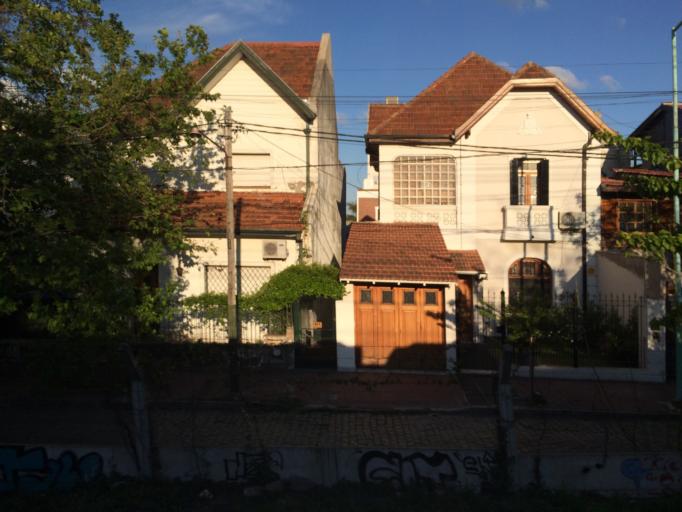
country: AR
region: Buenos Aires
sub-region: Partido de Lomas de Zamora
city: Lomas de Zamora
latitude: -34.7497
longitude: -58.3959
